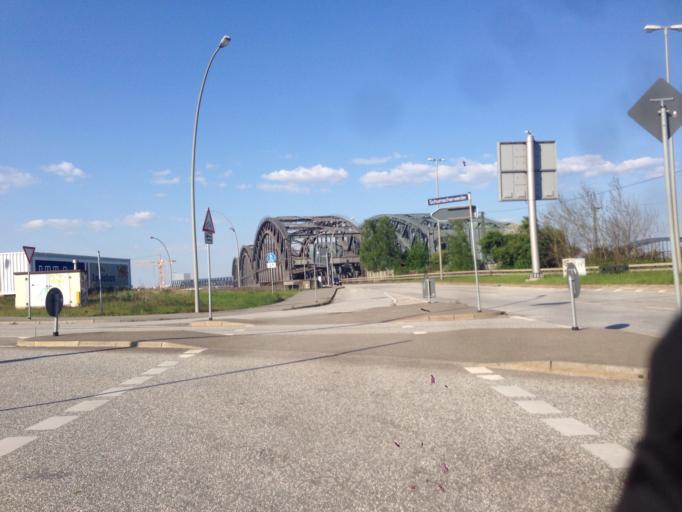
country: DE
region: Hamburg
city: Hammerbrook
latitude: 53.5309
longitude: 10.0198
